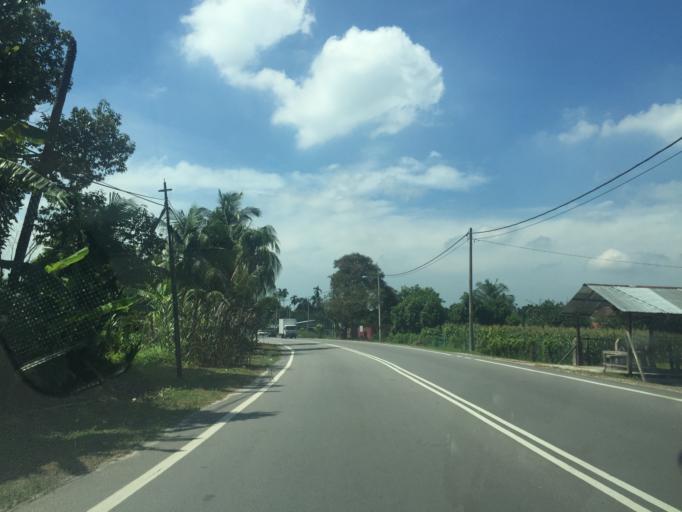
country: MY
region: Penang
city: Tasek Glugor
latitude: 5.5039
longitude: 100.5254
